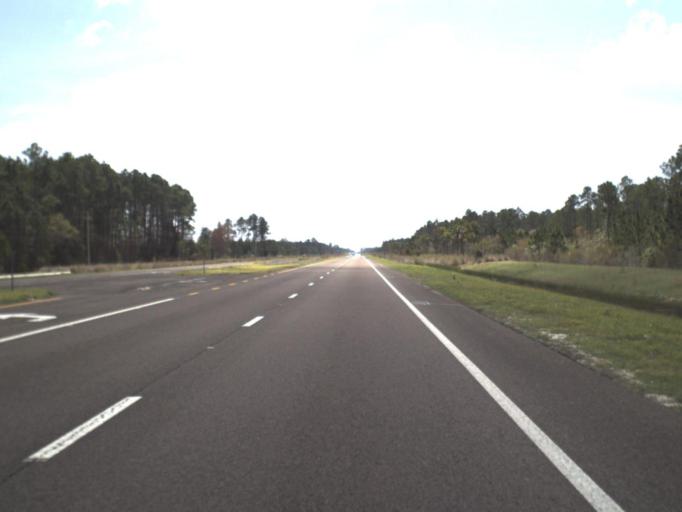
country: US
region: Florida
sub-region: Bay County
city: Laguna Beach
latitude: 30.2776
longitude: -85.8674
